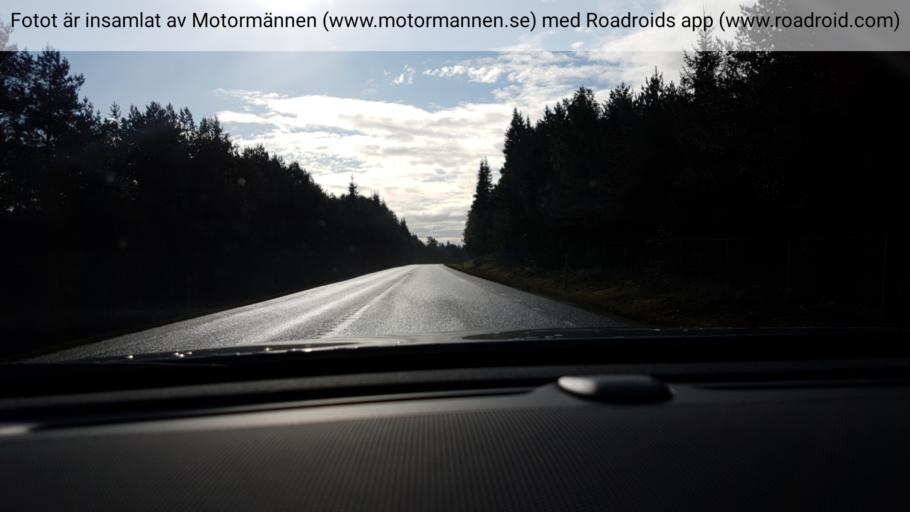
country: SE
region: Vaestra Goetaland
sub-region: Harryda Kommun
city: Hindas
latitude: 57.6693
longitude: 12.3604
